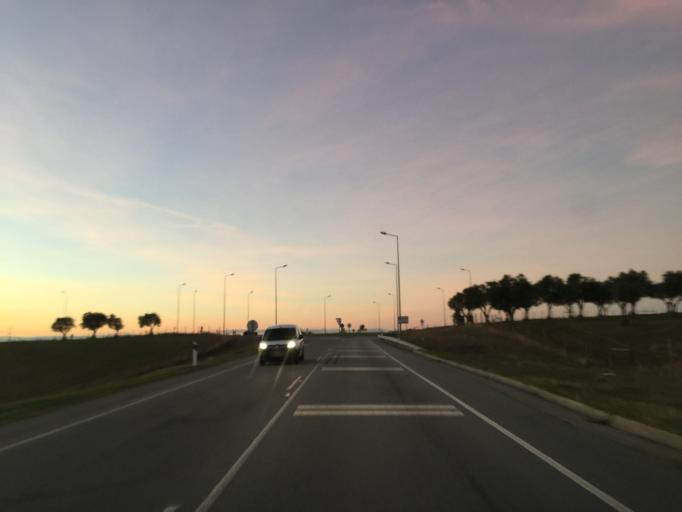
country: PT
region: Portalegre
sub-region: Alter do Chao
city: Alter do Chao
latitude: 39.3077
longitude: -7.6408
